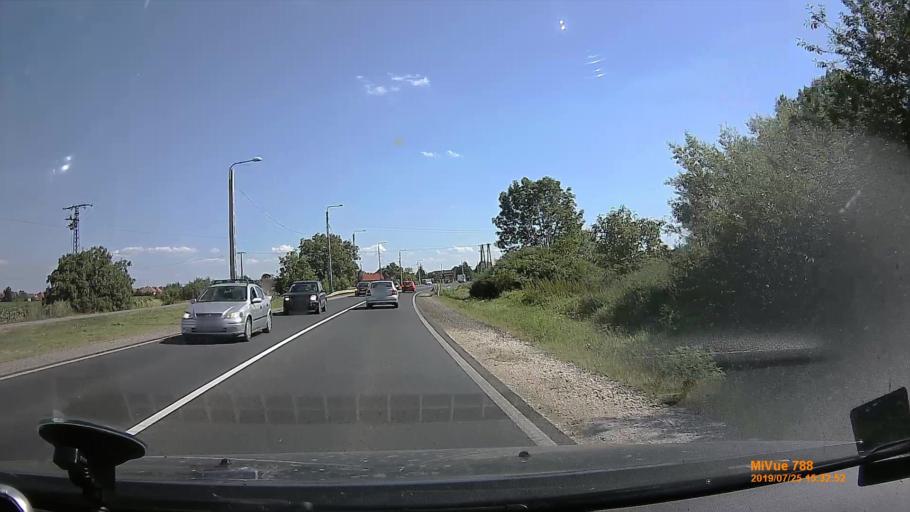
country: HU
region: Borsod-Abauj-Zemplen
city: Malyi
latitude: 48.0015
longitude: 20.8314
